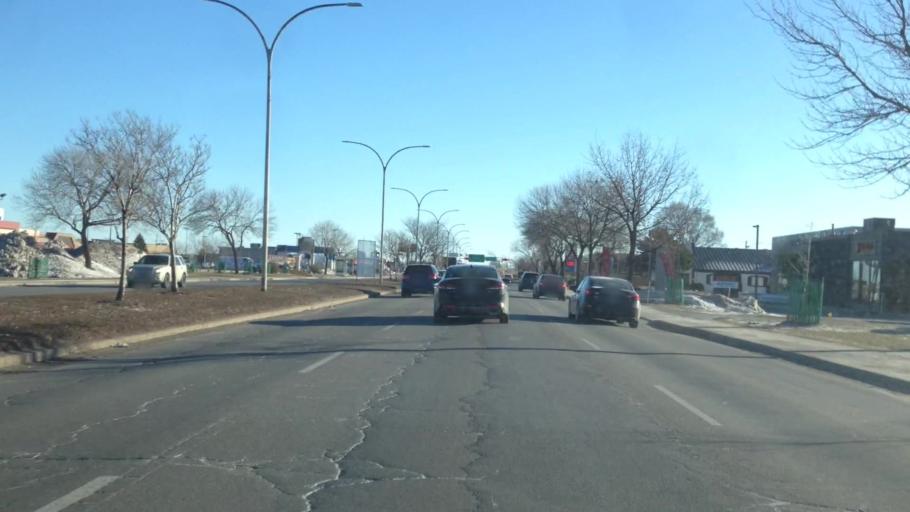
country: CA
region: Quebec
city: Dollard-Des Ormeaux
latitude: 45.4850
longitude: -73.7979
